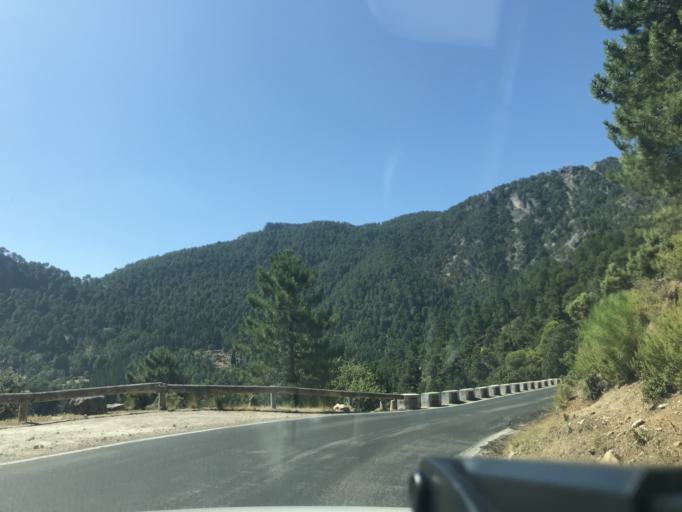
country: ES
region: Andalusia
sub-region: Provincia de Jaen
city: La Iruela
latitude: 37.9234
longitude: -2.9518
